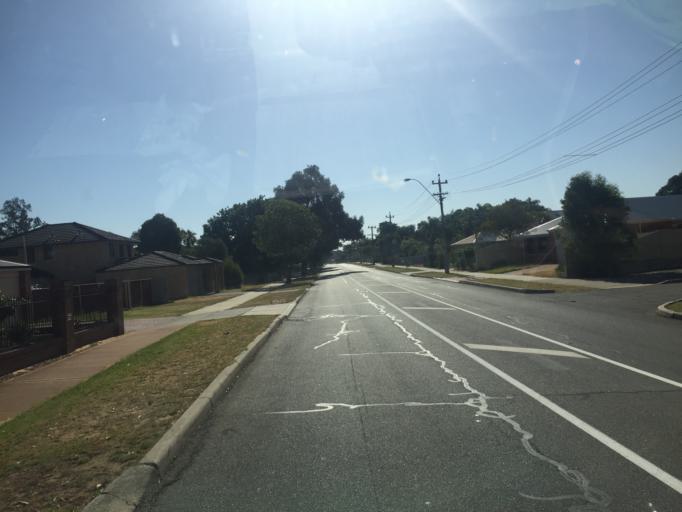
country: AU
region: Western Australia
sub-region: Gosnells
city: Kenwick
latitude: -32.0344
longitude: 115.9784
